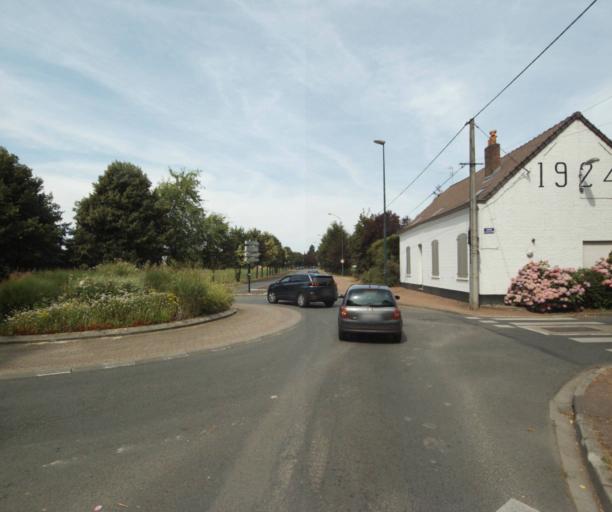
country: FR
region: Nord-Pas-de-Calais
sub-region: Departement du Nord
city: Mouvaux
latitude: 50.7147
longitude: 3.1182
